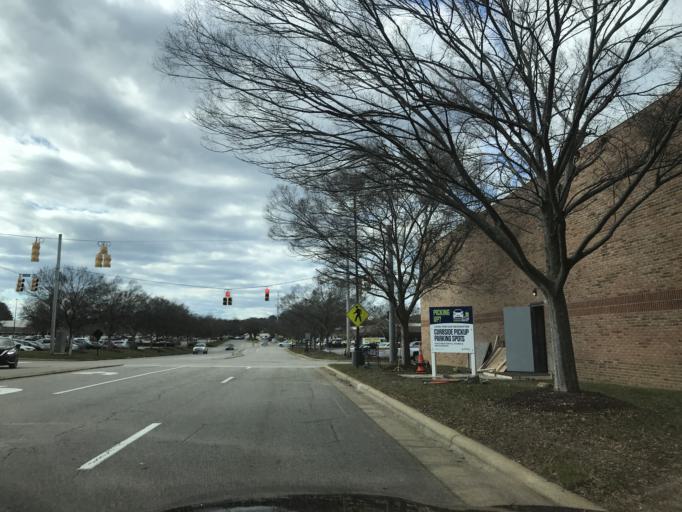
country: US
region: North Carolina
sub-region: Wake County
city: Cary
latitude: 35.7603
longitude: -78.7355
